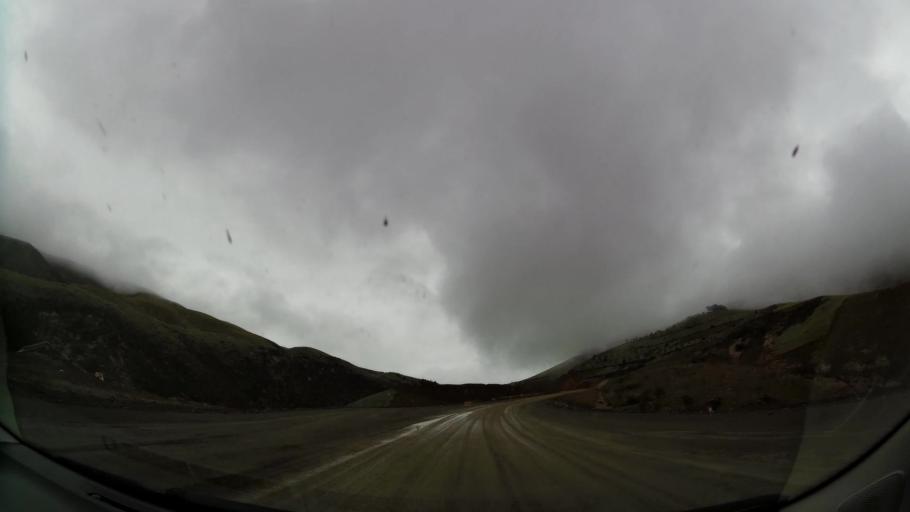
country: MA
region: Taza-Al Hoceima-Taounate
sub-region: Taza
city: Ajdir
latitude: 34.9114
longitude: -3.7967
